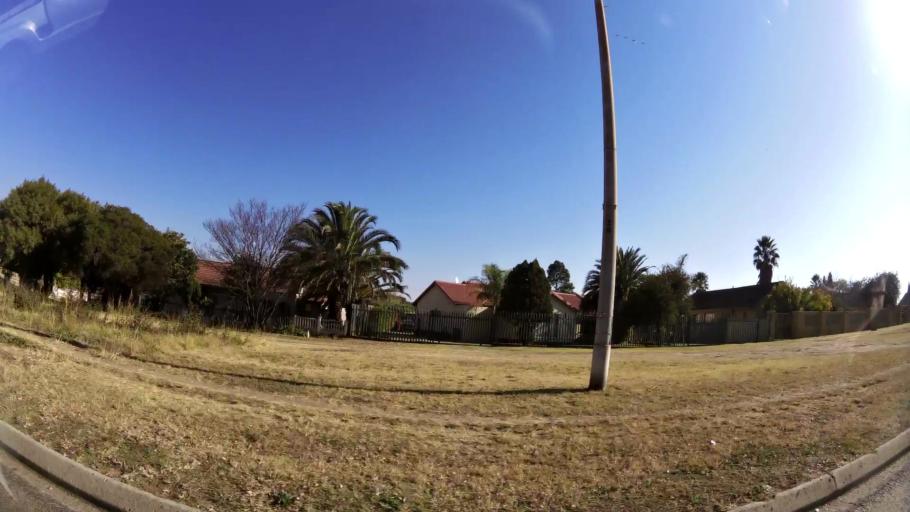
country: ZA
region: Gauteng
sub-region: City of Johannesburg Metropolitan Municipality
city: Modderfontein
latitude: -26.0586
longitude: 28.2009
